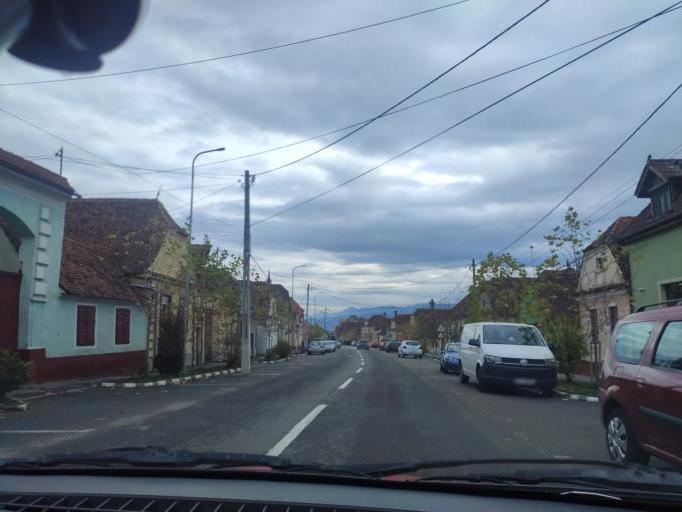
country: RO
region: Brasov
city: Codlea
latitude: 45.7013
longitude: 25.4422
